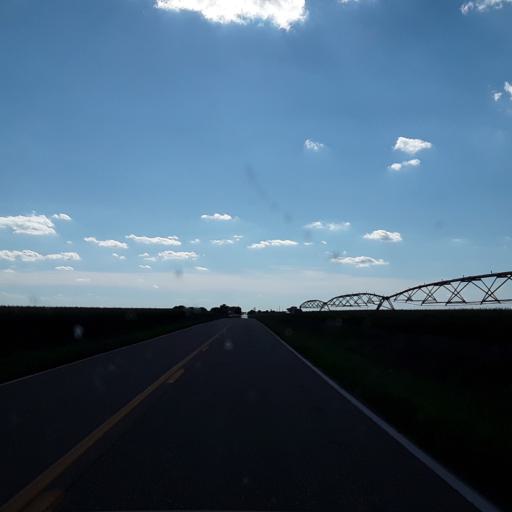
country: US
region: Nebraska
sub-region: Hall County
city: Wood River
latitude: 40.8877
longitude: -98.6204
